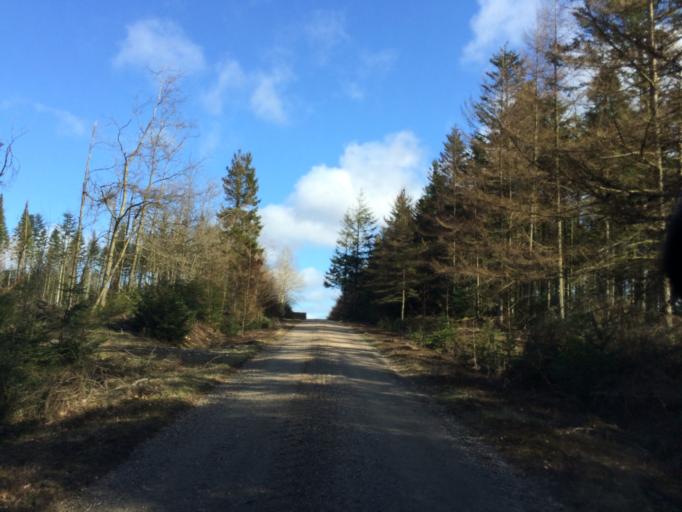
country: DK
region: Central Jutland
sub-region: Holstebro Kommune
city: Ulfborg
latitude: 56.2565
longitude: 8.4613
